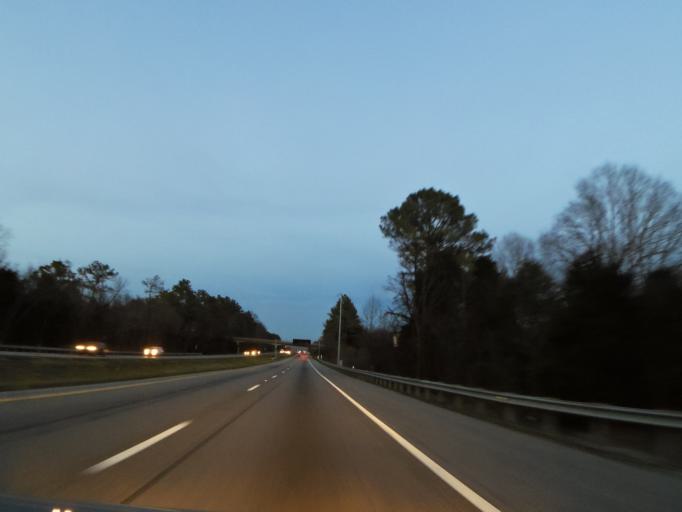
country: US
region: Tennessee
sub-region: Roane County
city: Kingston
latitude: 35.8650
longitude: -84.3893
